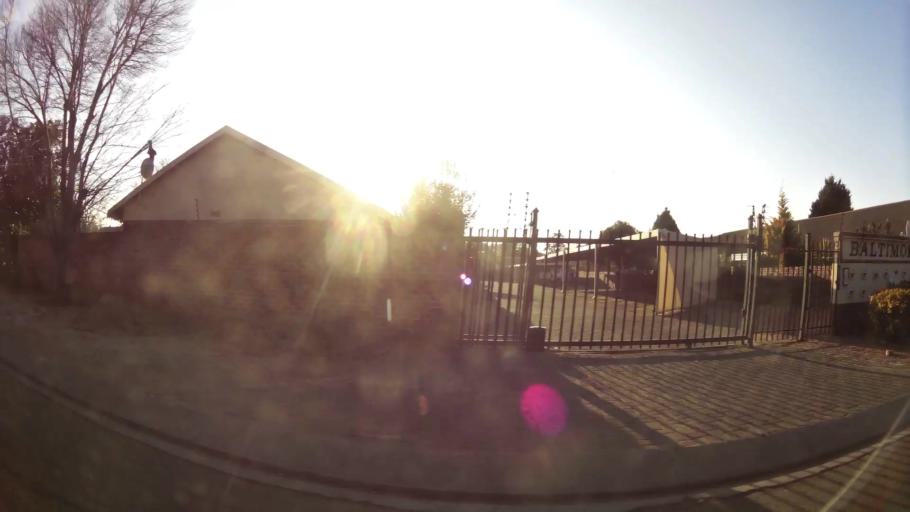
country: ZA
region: Orange Free State
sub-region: Mangaung Metropolitan Municipality
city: Bloemfontein
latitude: -29.1631
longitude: 26.1762
